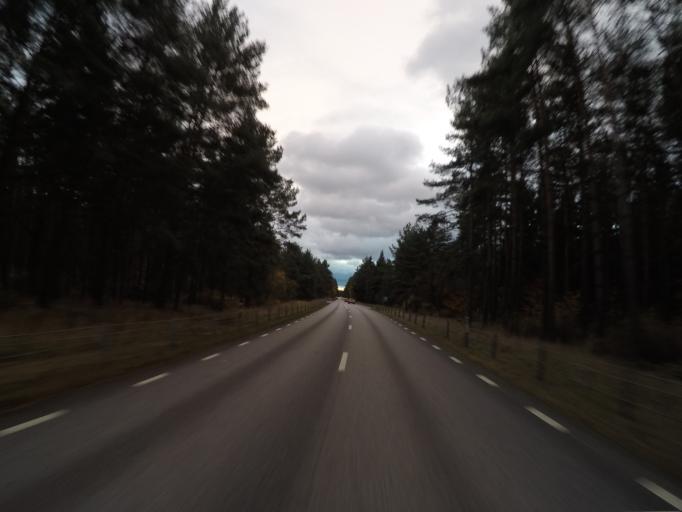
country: SE
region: Skane
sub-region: Kristianstads Kommun
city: Degeberga
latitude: 55.9162
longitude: 14.0727
